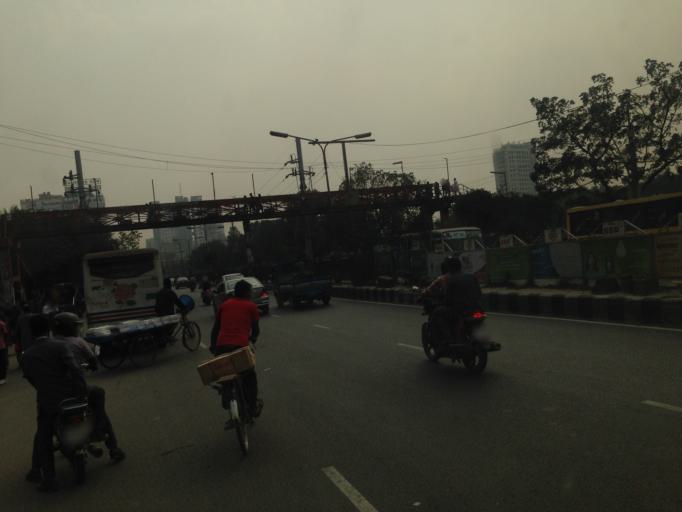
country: BD
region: Dhaka
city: Paltan
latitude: 23.7979
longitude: 90.4236
